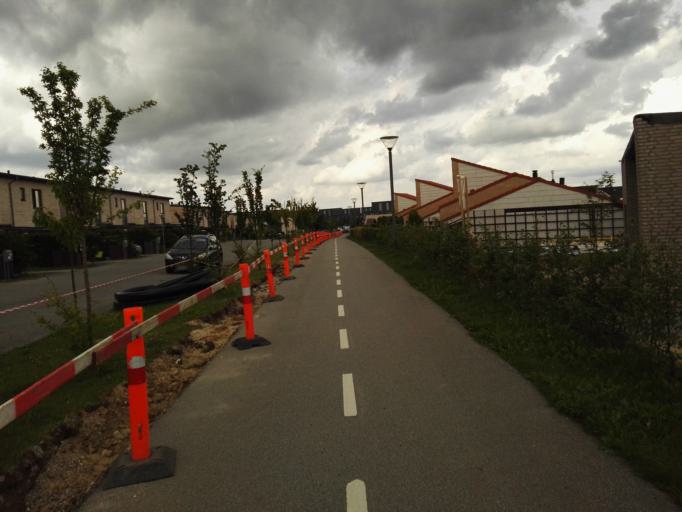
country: DK
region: Capital Region
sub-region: Egedal Kommune
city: Stenlose
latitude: 55.7618
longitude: 12.1759
